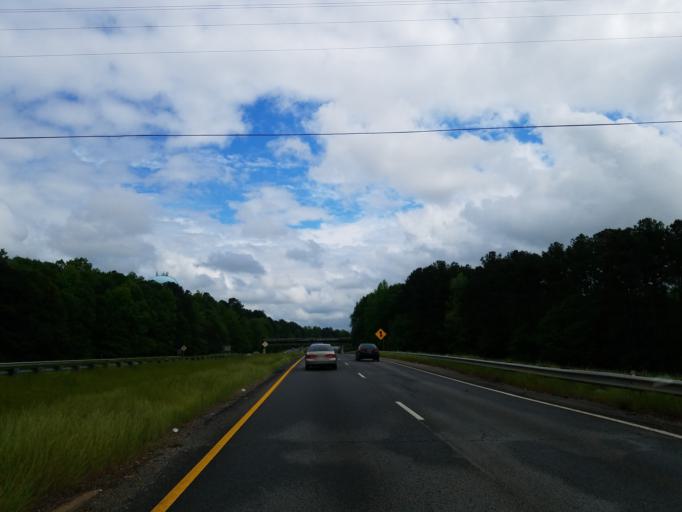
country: US
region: Georgia
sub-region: Spalding County
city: Griffin
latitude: 33.2301
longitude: -84.2918
